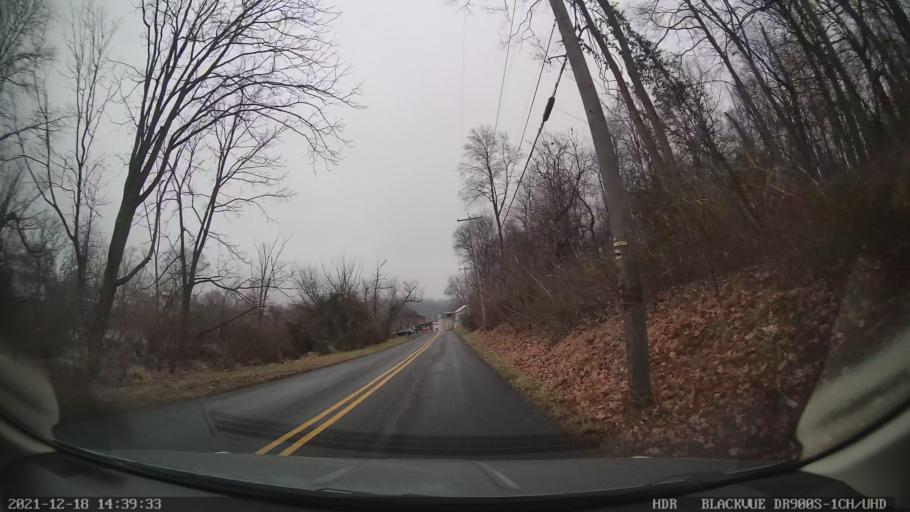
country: US
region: Pennsylvania
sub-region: Berks County
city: New Berlinville
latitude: 40.3741
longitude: -75.6323
